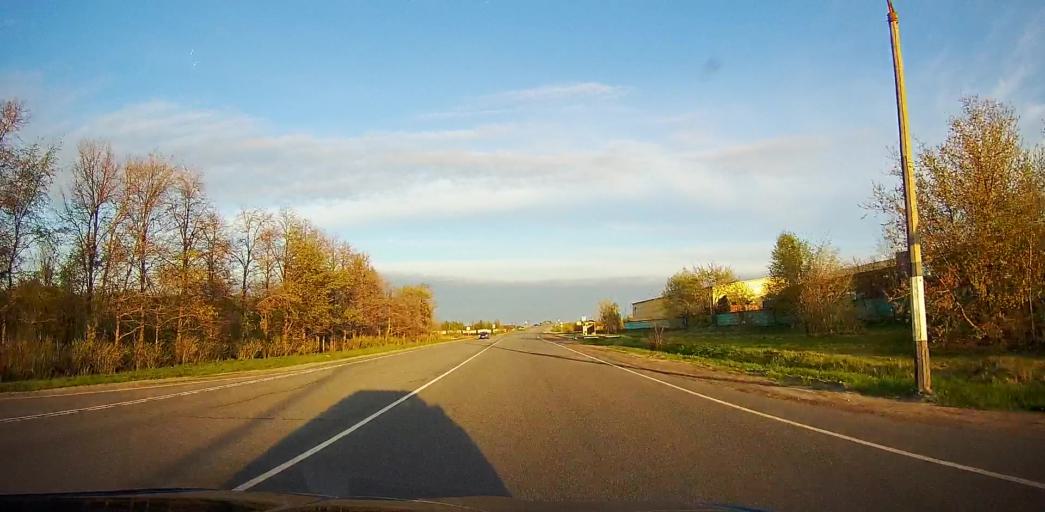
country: RU
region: Moskovskaya
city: Troitskoye
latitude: 55.2200
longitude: 38.5825
